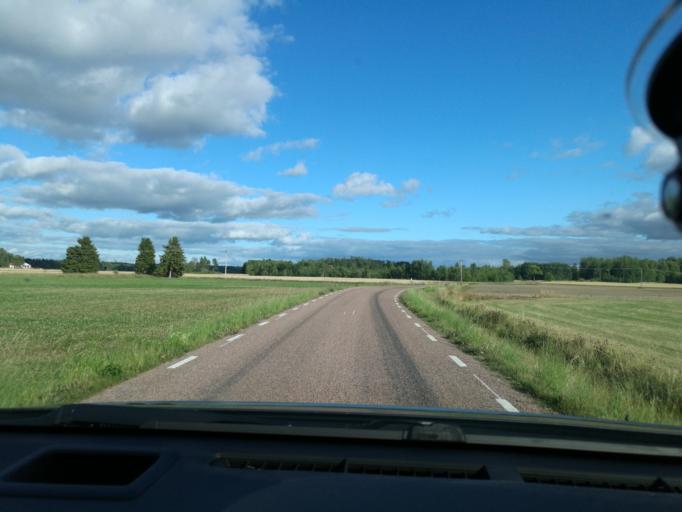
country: SE
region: Vaestmanland
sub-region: Hallstahammars Kommun
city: Hallstahammar
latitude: 59.5448
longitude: 16.1254
